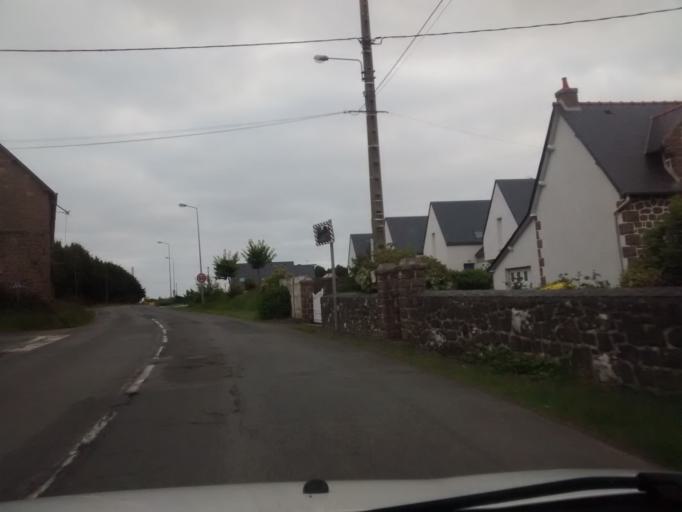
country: FR
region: Brittany
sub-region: Departement des Cotes-d'Armor
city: Tregastel
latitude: 48.8105
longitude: -3.4748
